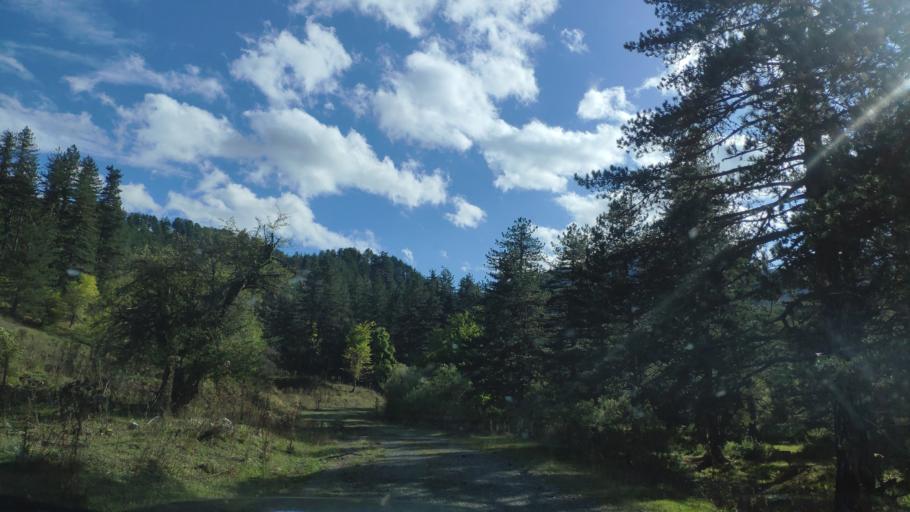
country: AL
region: Korce
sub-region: Rrethi i Devollit
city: Miras
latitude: 40.3975
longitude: 20.8817
